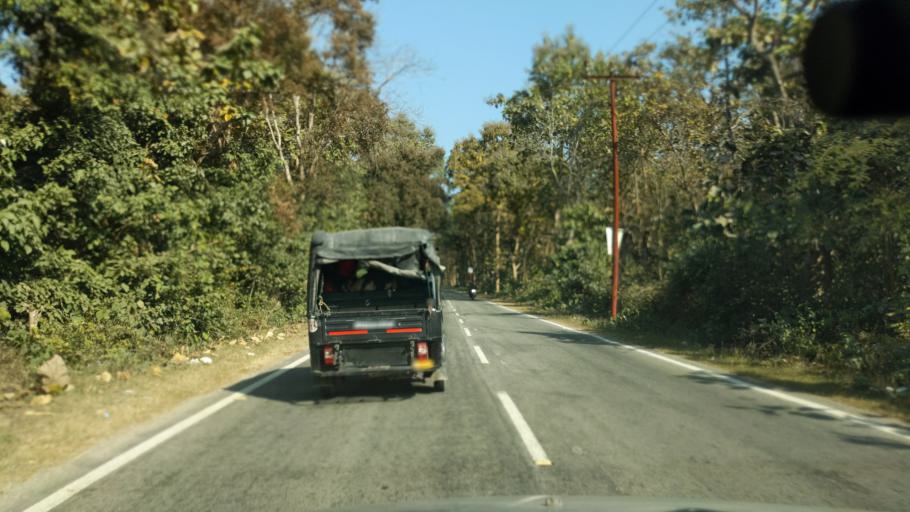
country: IN
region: Uttarakhand
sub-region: Naini Tal
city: Ramnagar
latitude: 29.3799
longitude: 79.1428
